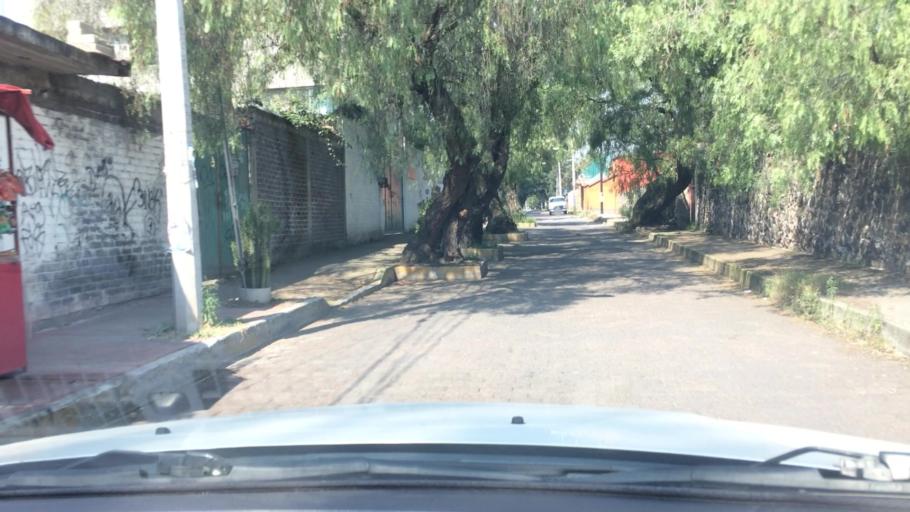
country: MX
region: Mexico City
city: Xochimilco
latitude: 19.2618
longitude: -99.1335
